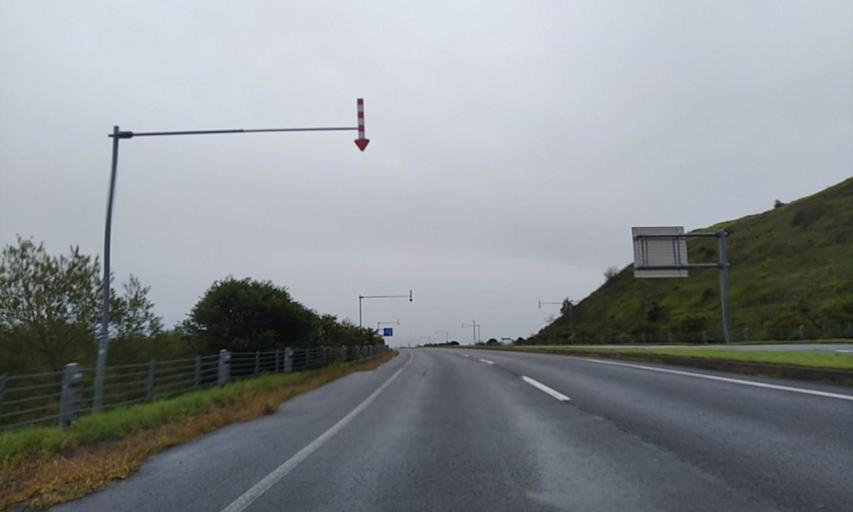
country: JP
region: Hokkaido
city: Kushiro
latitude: 43.0173
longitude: 144.2567
